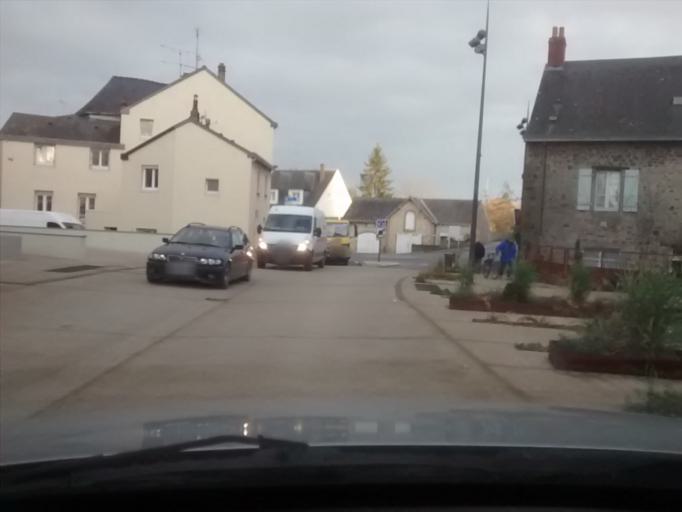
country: FR
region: Pays de la Loire
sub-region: Departement de la Mayenne
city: Change
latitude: 48.0993
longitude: -0.7891
